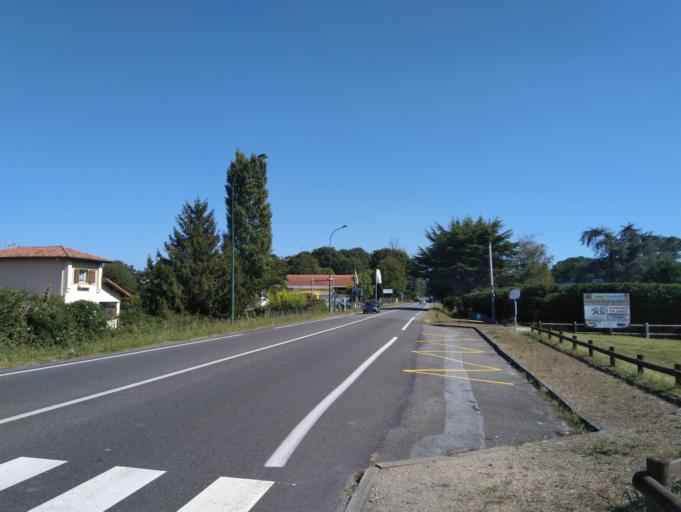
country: FR
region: Aquitaine
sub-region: Departement des Landes
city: Narrosse
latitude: 43.6971
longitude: -1.0205
